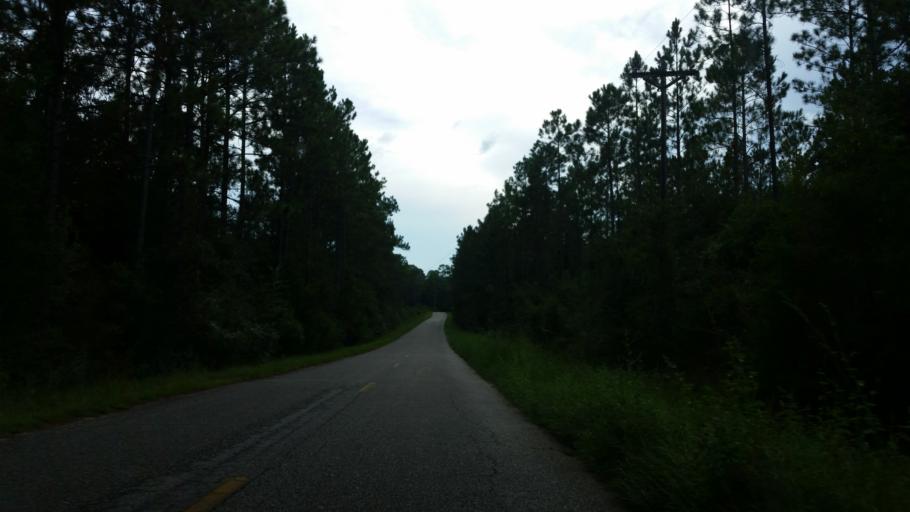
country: US
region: Florida
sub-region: Santa Rosa County
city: Point Baker
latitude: 30.7296
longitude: -86.8943
